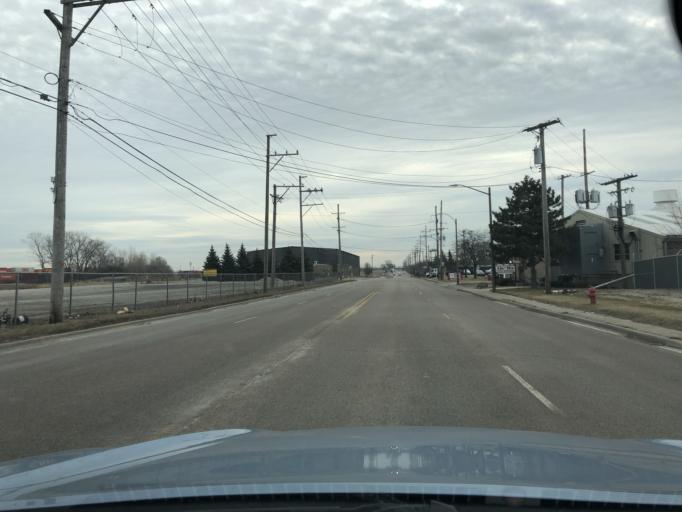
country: US
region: Illinois
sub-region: DuPage County
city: Bensenville
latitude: 41.9522
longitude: -87.9290
